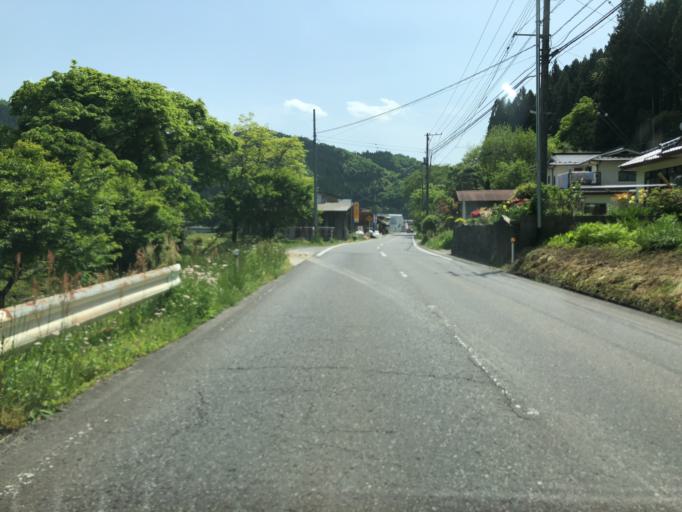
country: JP
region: Fukushima
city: Ishikawa
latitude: 37.1495
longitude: 140.4783
